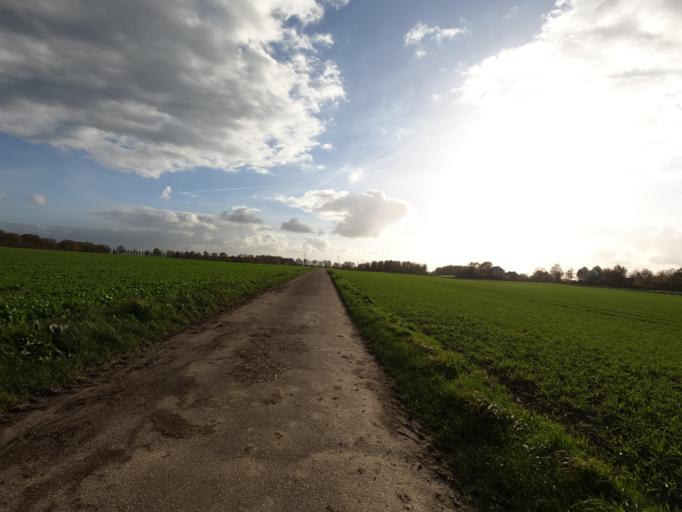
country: DE
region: North Rhine-Westphalia
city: Geilenkirchen
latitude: 50.9573
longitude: 6.1323
